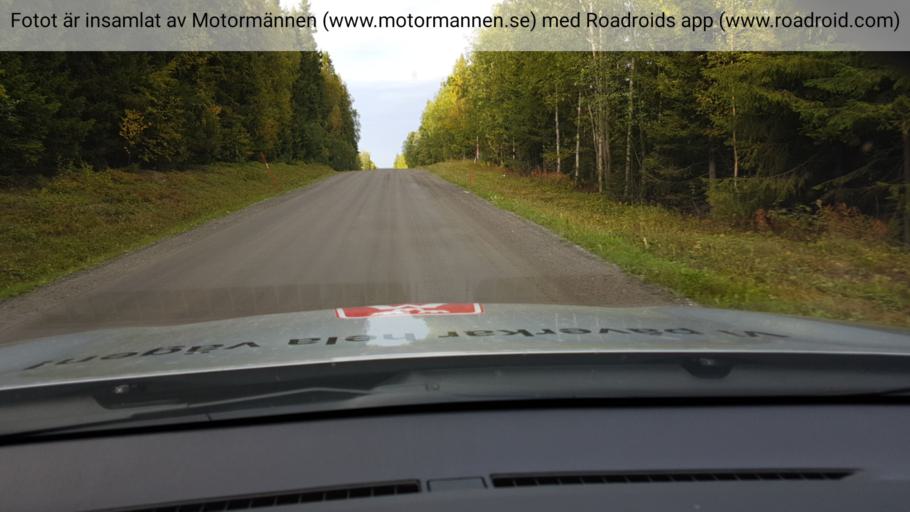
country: SE
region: Jaemtland
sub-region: Stroemsunds Kommun
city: Stroemsund
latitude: 64.0045
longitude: 15.8154
